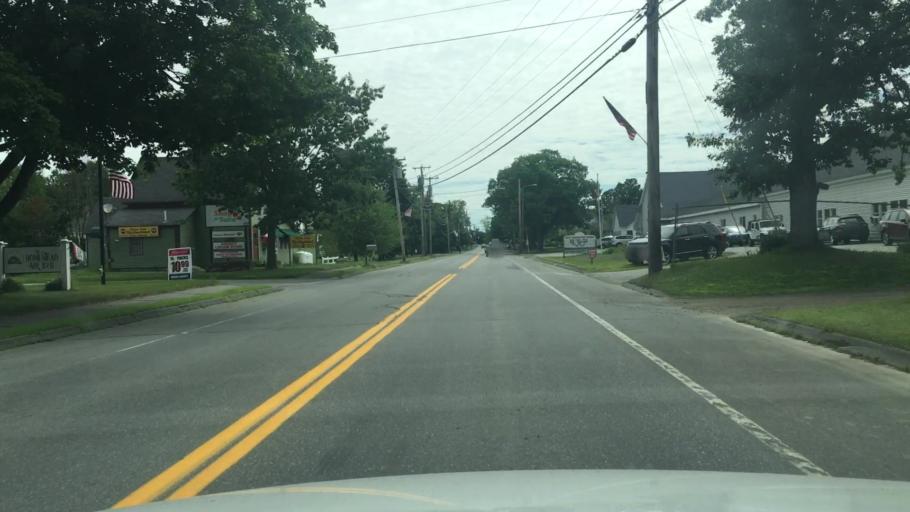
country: US
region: Maine
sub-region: Waldo County
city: Troy
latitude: 44.6120
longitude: -69.3396
